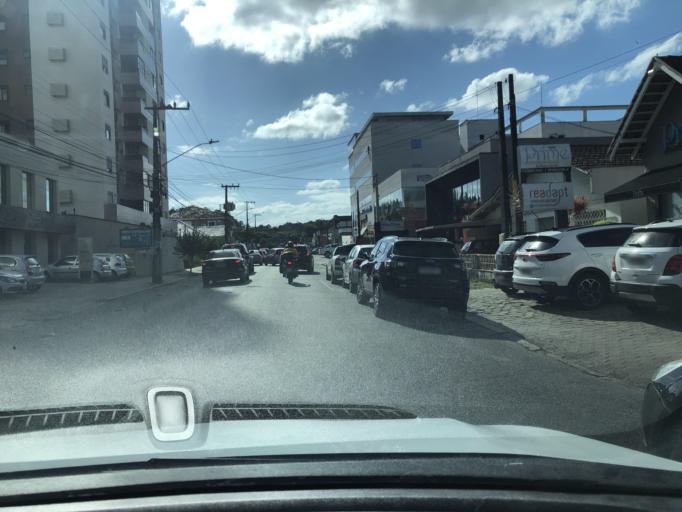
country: BR
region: Santa Catarina
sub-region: Joinville
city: Joinville
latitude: -26.2968
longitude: -48.8491
